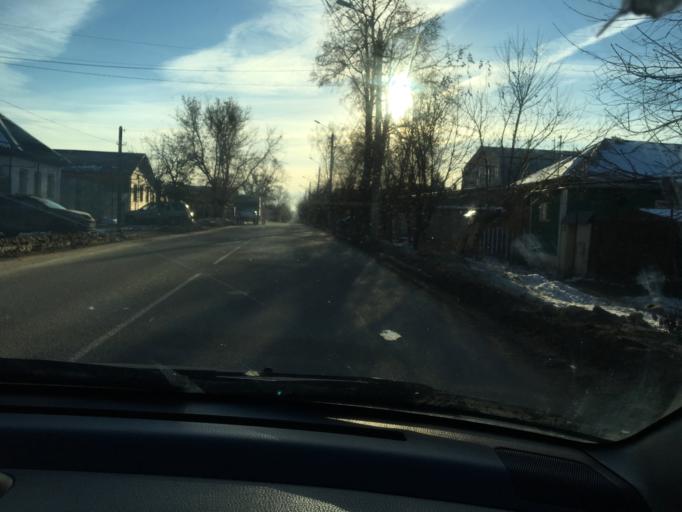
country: RU
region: Tula
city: Tula
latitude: 54.2196
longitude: 37.5978
